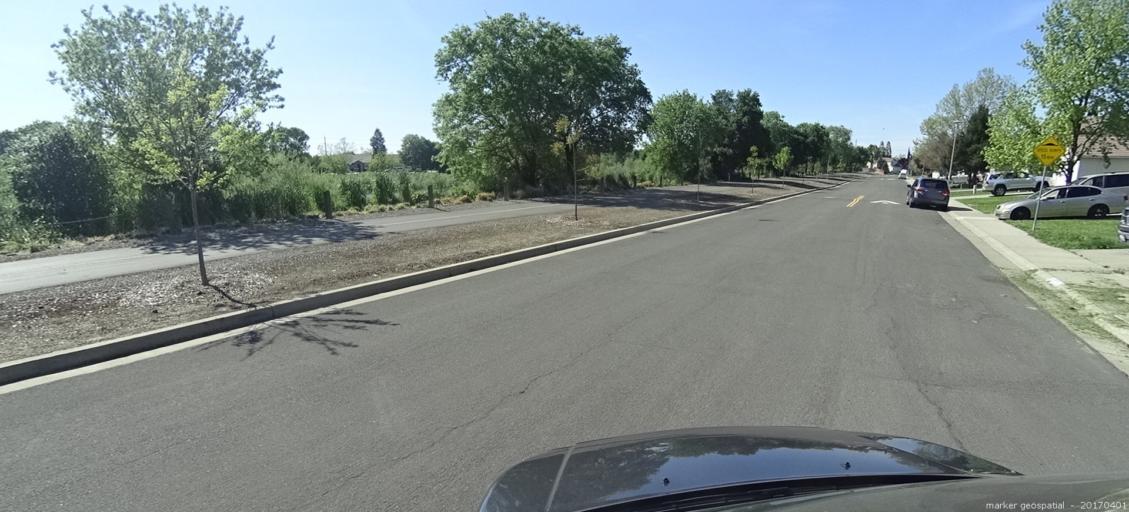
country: US
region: California
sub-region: Sacramento County
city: Laguna
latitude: 38.4454
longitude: -121.4415
